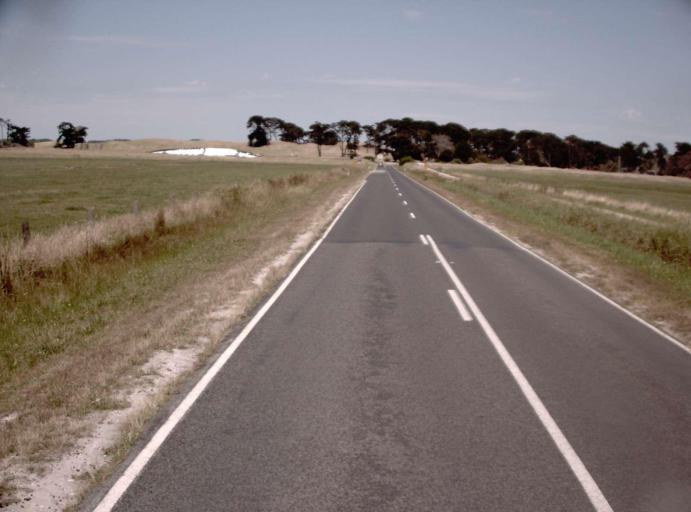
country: AU
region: Victoria
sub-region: Bass Coast
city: North Wonthaggi
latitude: -38.6995
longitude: 145.8383
